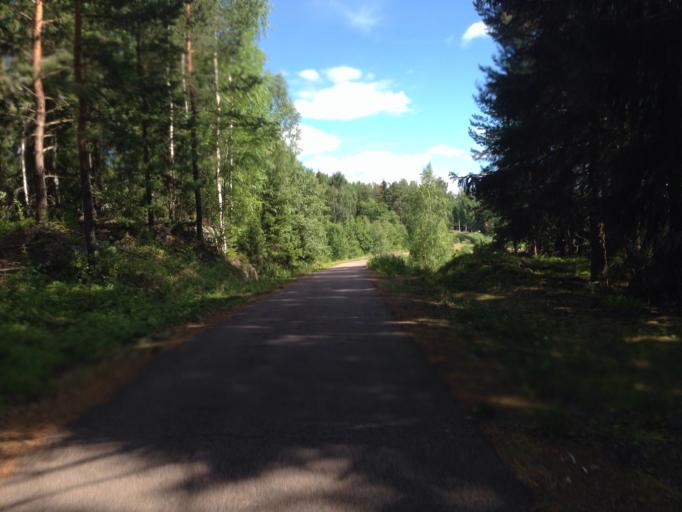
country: SE
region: Dalarna
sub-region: Ludvika Kommun
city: Grangesberg
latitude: 60.2143
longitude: 15.0442
